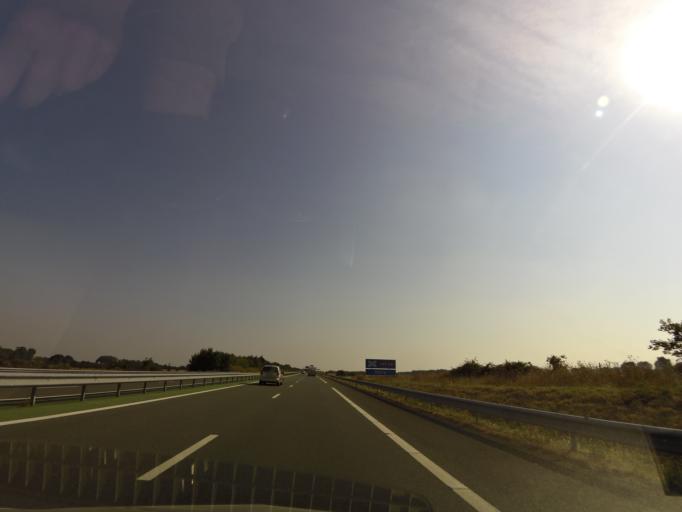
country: FR
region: Pays de la Loire
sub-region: Departement de la Vendee
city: Les Essarts
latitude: 46.8003
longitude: -1.2222
